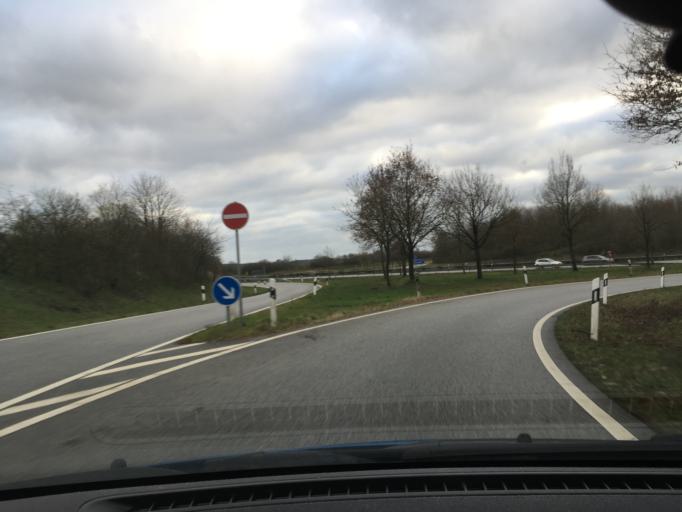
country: DE
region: Schleswig-Holstein
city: Besdorf
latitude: 54.0597
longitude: 9.3649
